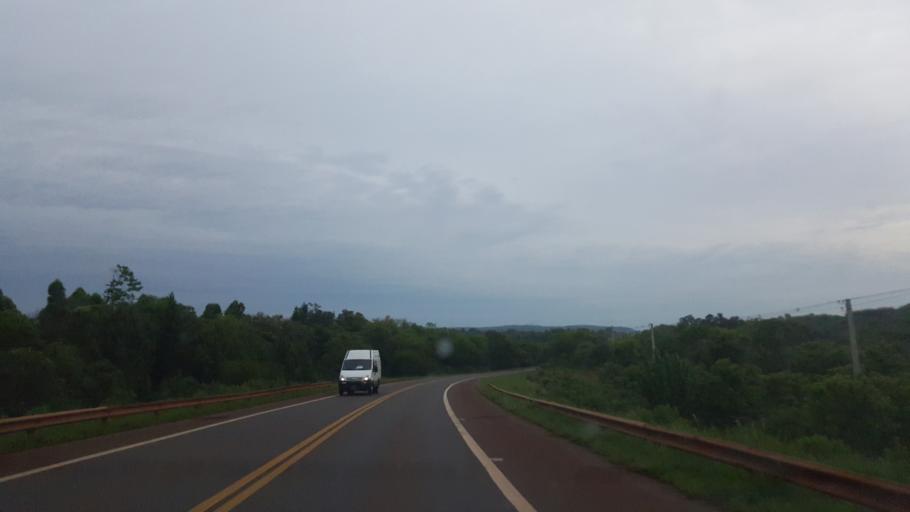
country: AR
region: Misiones
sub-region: Departamento de Apostoles
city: San Jose
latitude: -27.7666
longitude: -55.8016
